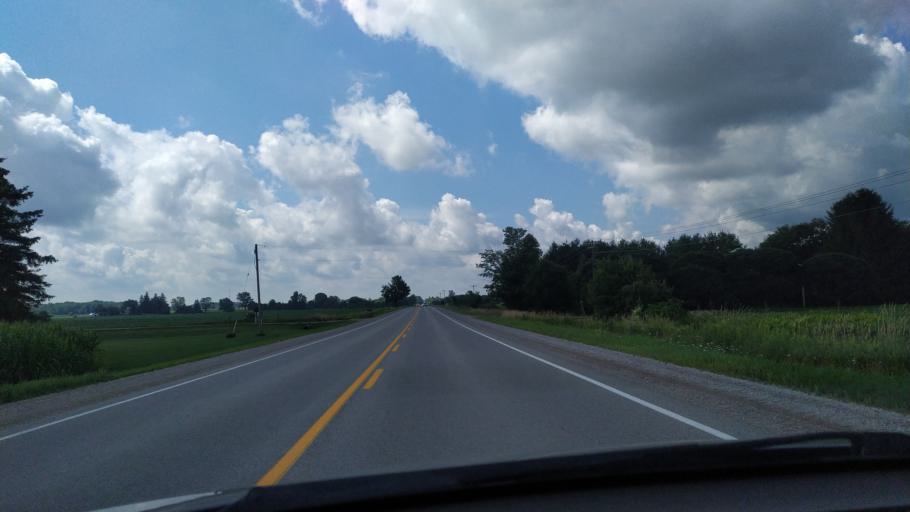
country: CA
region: Ontario
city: South Huron
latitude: 43.3468
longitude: -81.2946
